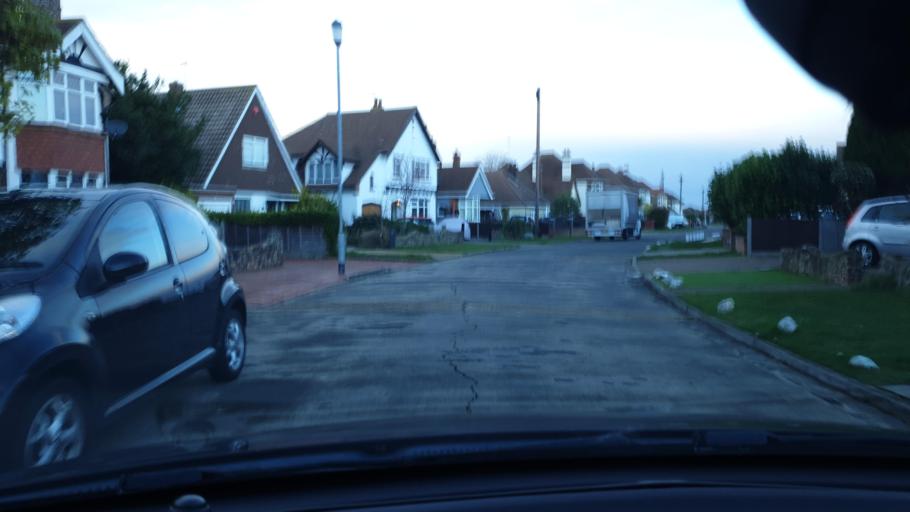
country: GB
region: England
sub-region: Essex
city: Clacton-on-Sea
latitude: 51.7972
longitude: 1.1651
